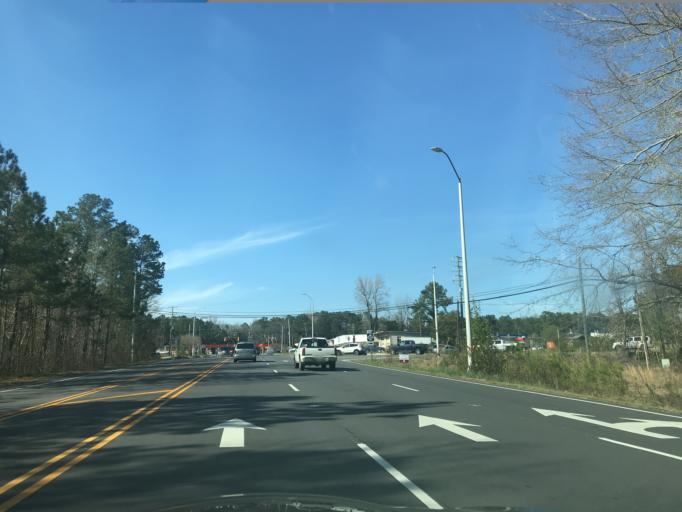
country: US
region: North Carolina
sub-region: Wake County
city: Fuquay-Varina
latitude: 35.5948
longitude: -78.7587
